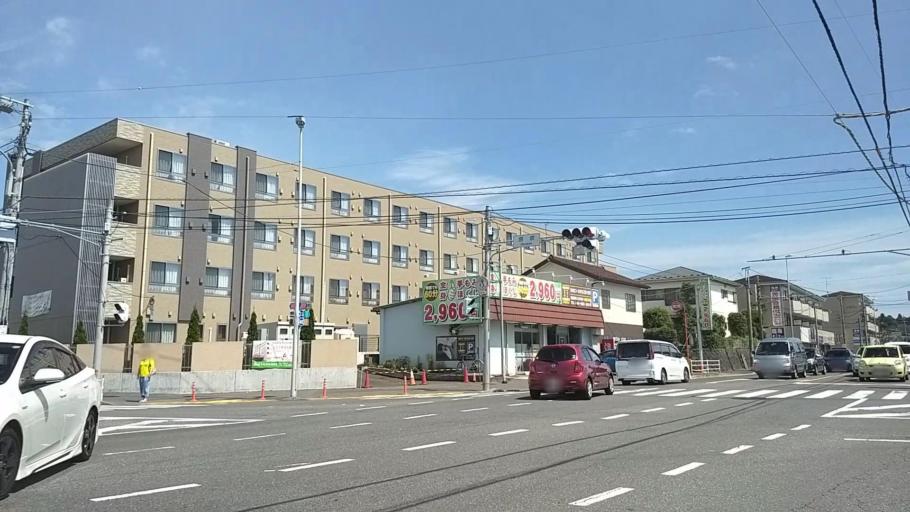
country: JP
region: Kanagawa
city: Fujisawa
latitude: 35.3771
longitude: 139.5053
